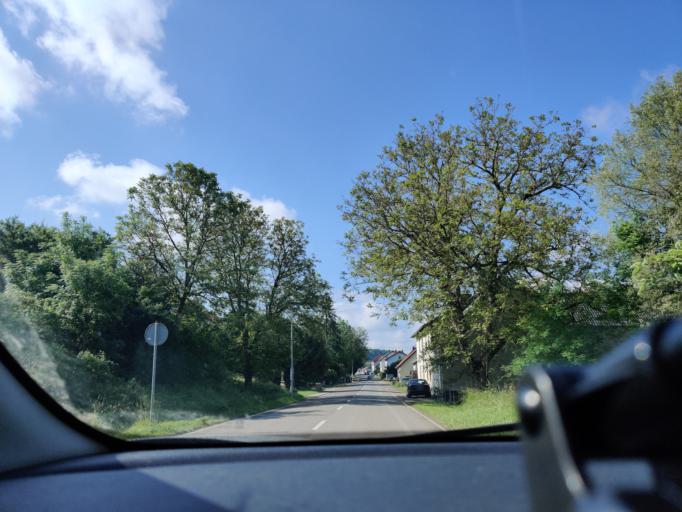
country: DE
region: Saarland
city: Gersheim
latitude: 49.1722
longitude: 7.1614
